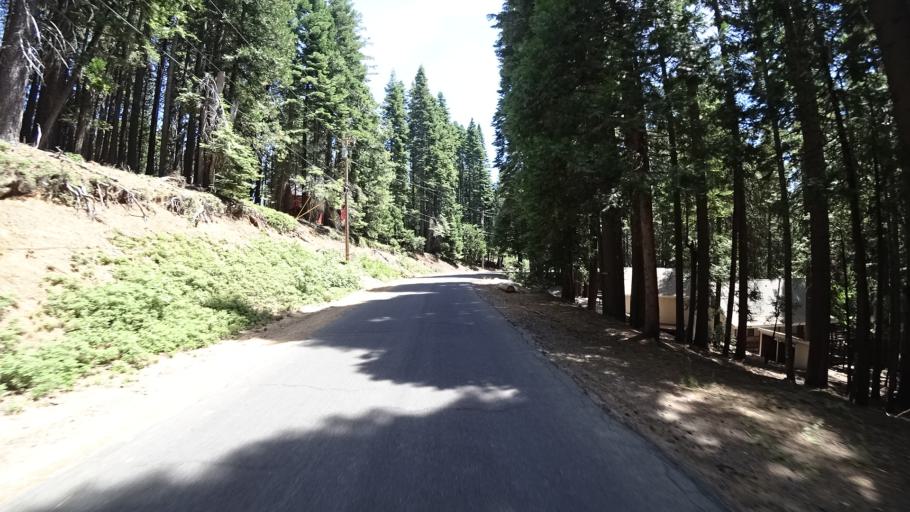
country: US
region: California
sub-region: Calaveras County
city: Arnold
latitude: 38.3077
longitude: -120.2647
